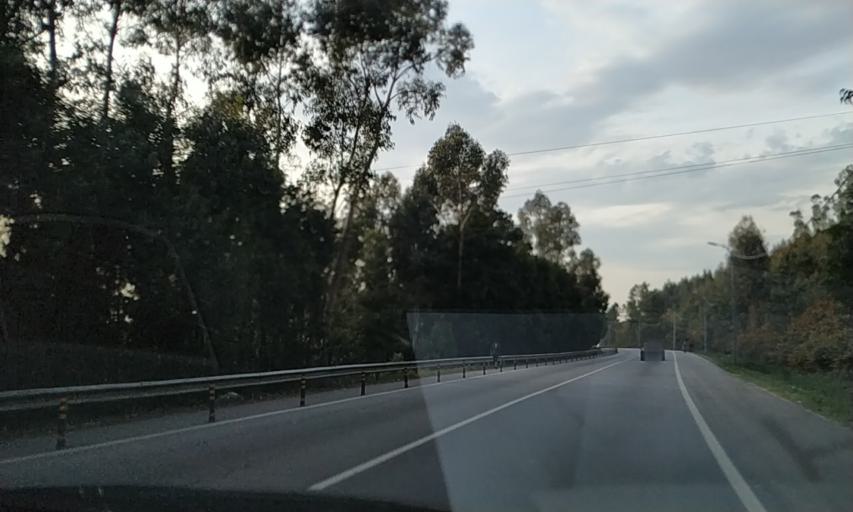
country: PT
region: Porto
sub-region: Valongo
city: Valongo
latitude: 41.1979
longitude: -8.5230
